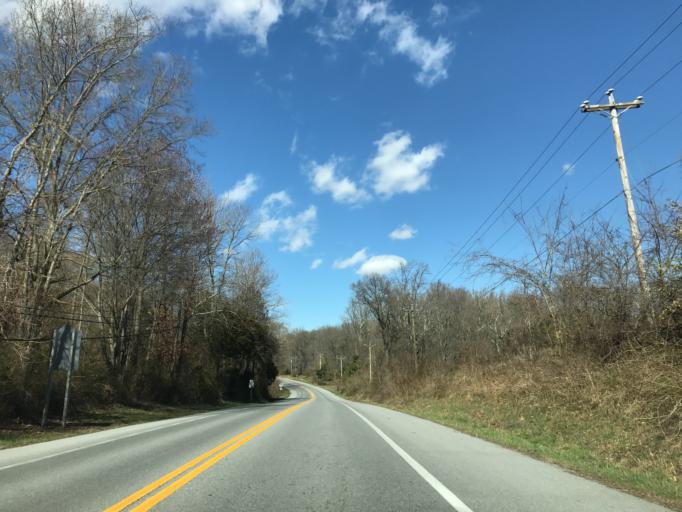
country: US
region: Maryland
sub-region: Queen Anne's County
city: Kingstown
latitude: 39.1315
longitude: -75.9760
